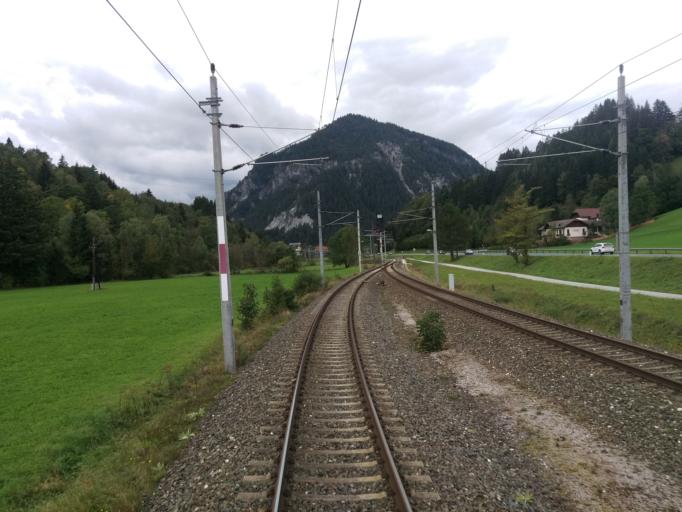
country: AT
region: Styria
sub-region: Politischer Bezirk Liezen
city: Schladming
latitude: 47.3880
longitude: 13.6088
